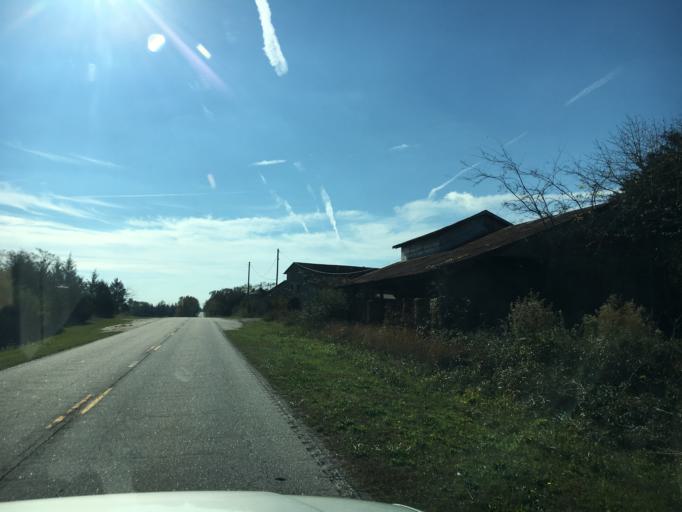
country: US
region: South Carolina
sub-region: Anderson County
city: Iva
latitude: 34.3682
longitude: -82.7123
